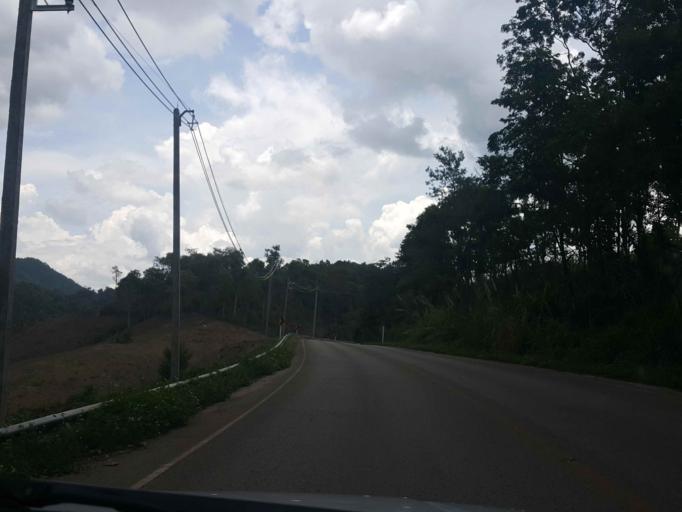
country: TH
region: Lampang
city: Ngao
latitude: 18.9322
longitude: 100.0897
